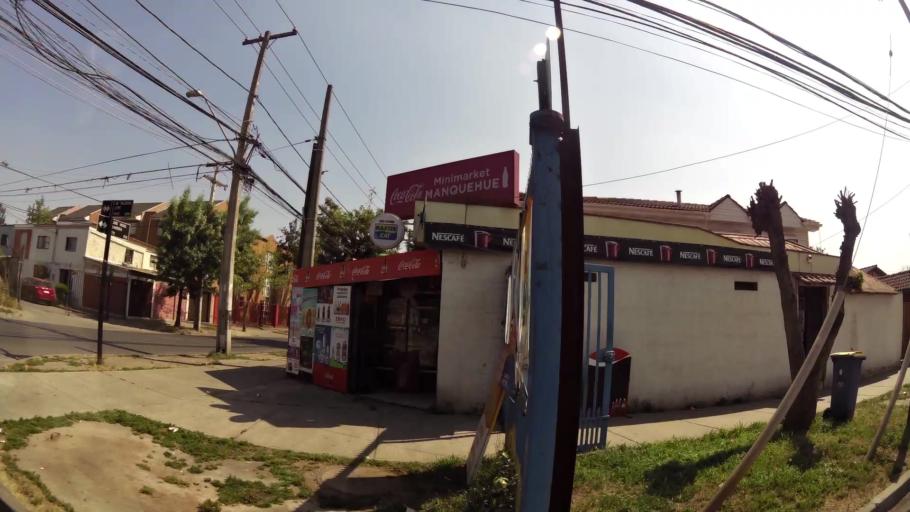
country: CL
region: Santiago Metropolitan
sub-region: Provincia de Santiago
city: La Pintana
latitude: -33.5502
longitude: -70.5972
